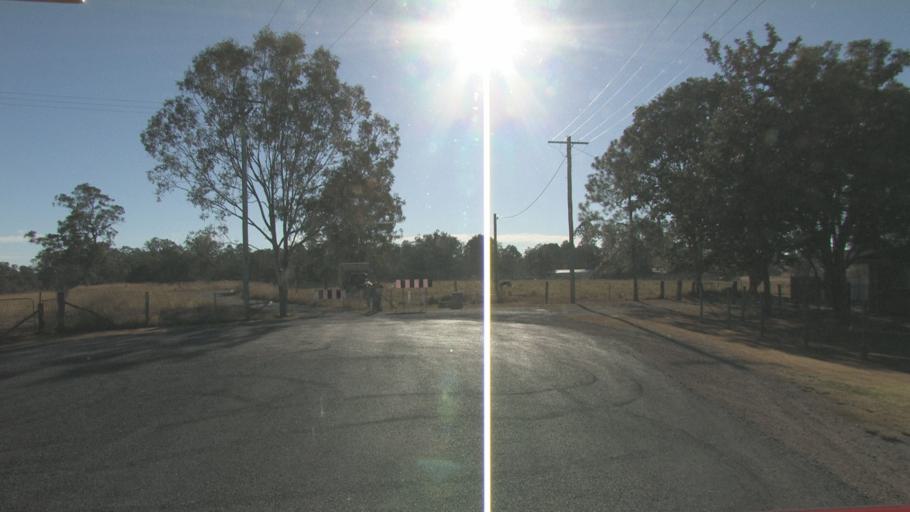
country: AU
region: Queensland
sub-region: Logan
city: North Maclean
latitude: -27.7979
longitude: 153.0068
